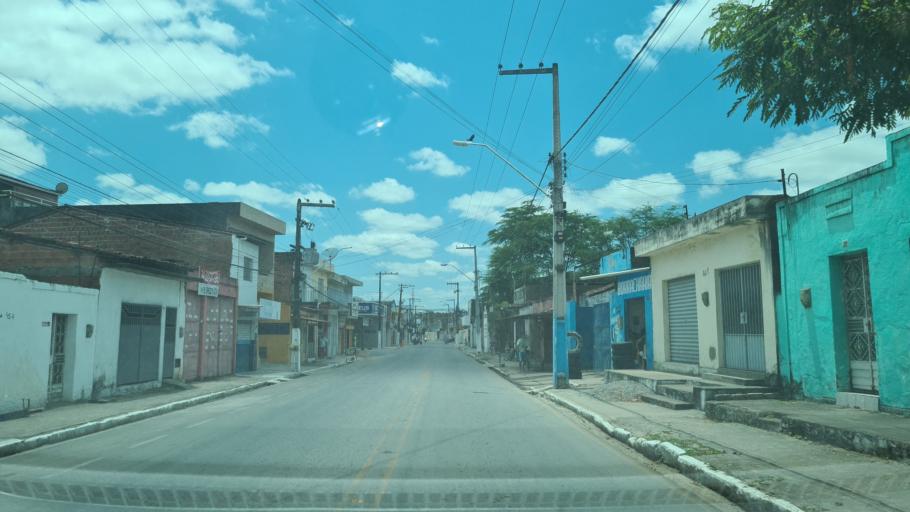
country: BR
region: Alagoas
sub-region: Uniao Dos Palmares
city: Uniao dos Palmares
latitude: -9.1629
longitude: -36.0282
